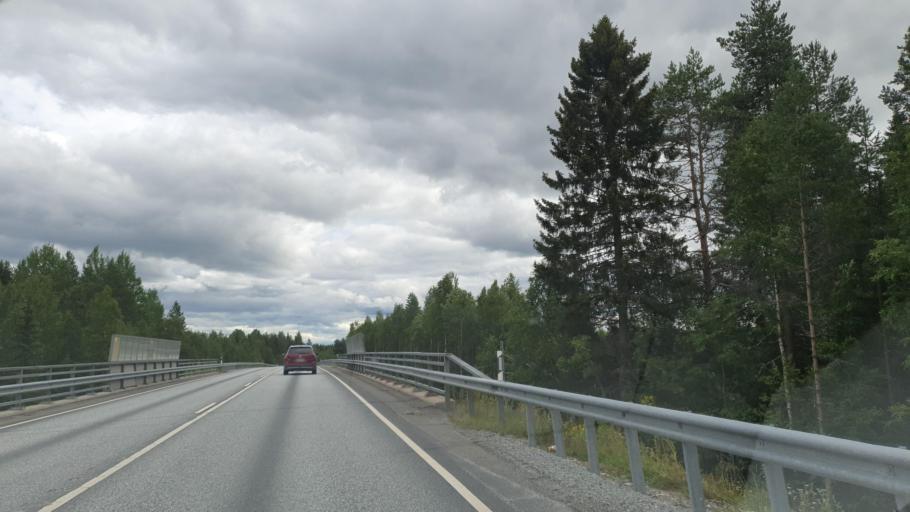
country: FI
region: Northern Savo
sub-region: Ylae-Savo
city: Sonkajaervi
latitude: 63.8888
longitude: 27.4305
